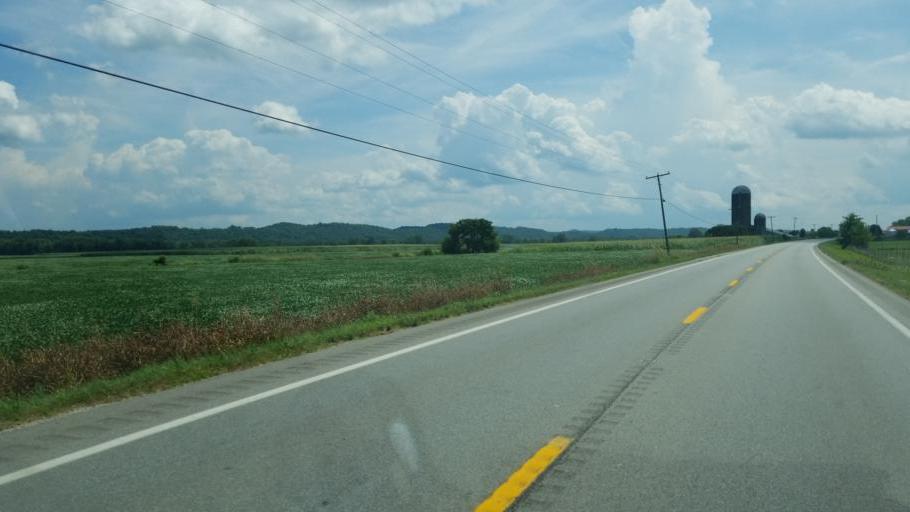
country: US
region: West Virginia
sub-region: Putnam County
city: Buffalo
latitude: 38.7375
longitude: -81.9758
